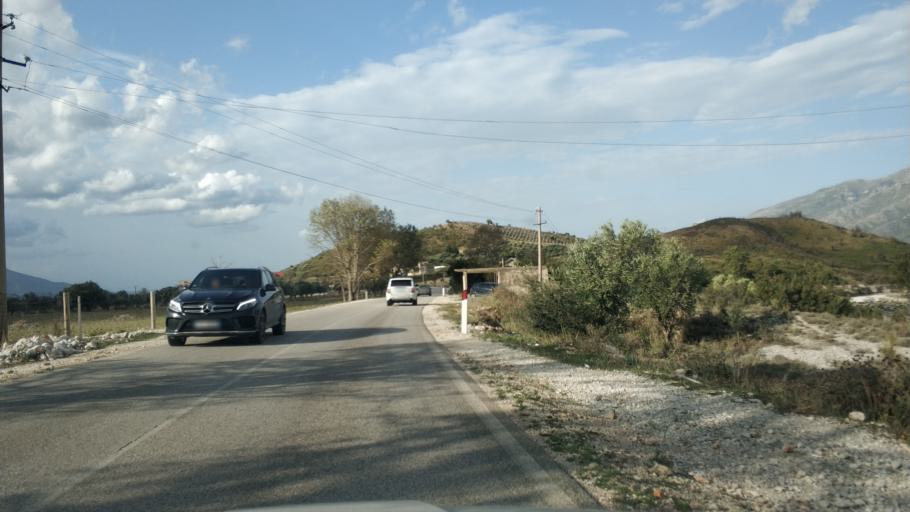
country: AL
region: Vlore
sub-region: Rrethi i Vlores
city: Orikum
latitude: 40.2934
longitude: 19.4909
